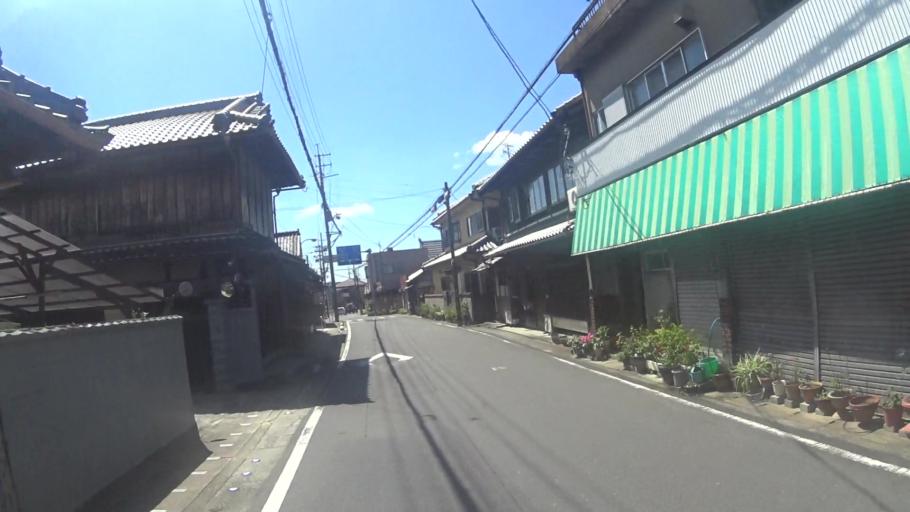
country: JP
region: Nara
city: Nara-shi
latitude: 34.7405
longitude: 135.8380
